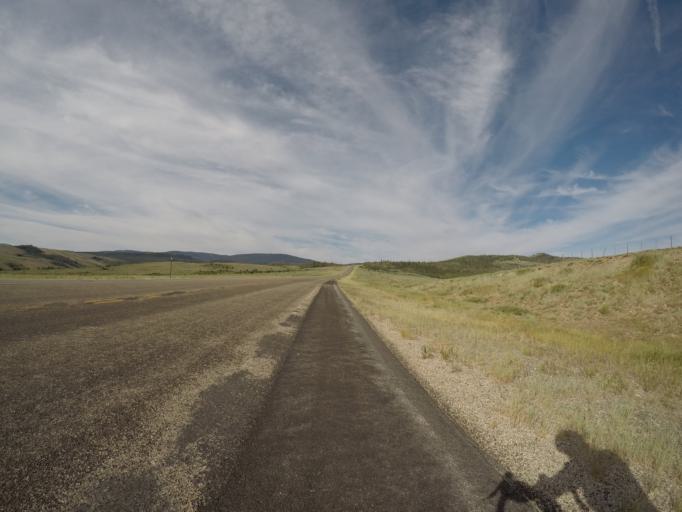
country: US
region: Wyoming
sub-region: Carbon County
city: Saratoga
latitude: 41.1883
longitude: -106.8554
